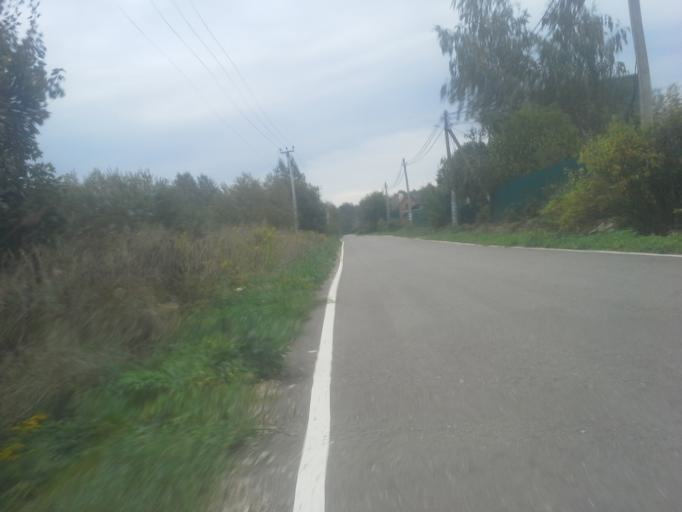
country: RU
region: Moskovskaya
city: Kievskij
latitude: 55.3510
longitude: 36.9078
